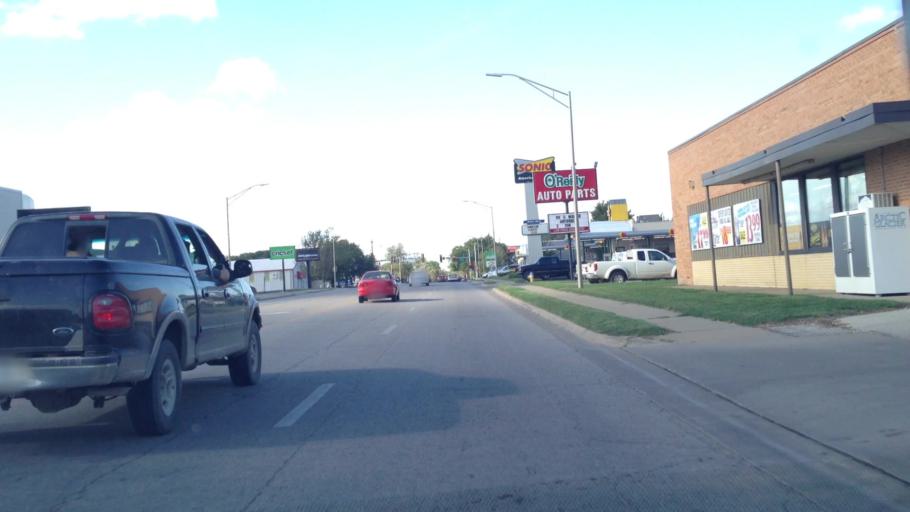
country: US
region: Kansas
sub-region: Franklin County
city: Ottawa
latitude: 38.5918
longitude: -95.2687
